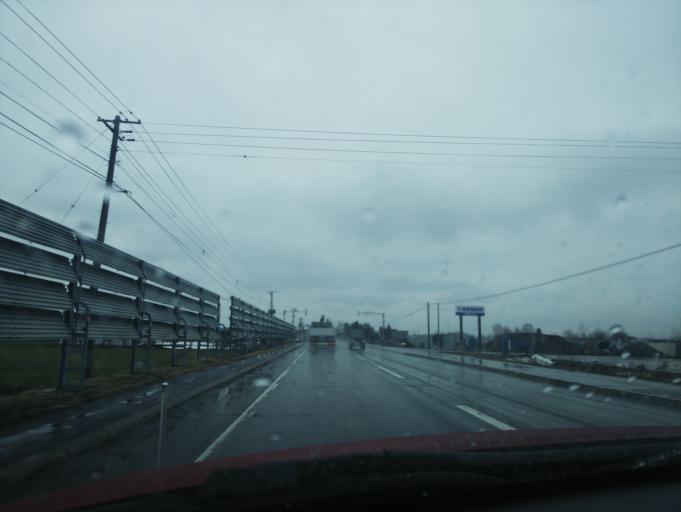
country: JP
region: Hokkaido
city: Nayoro
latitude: 44.2068
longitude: 142.3949
